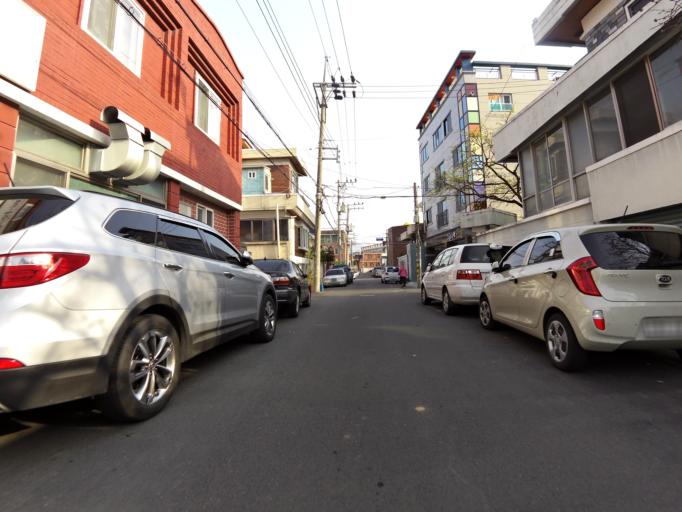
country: KR
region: Daegu
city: Daegu
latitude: 35.8713
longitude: 128.6470
